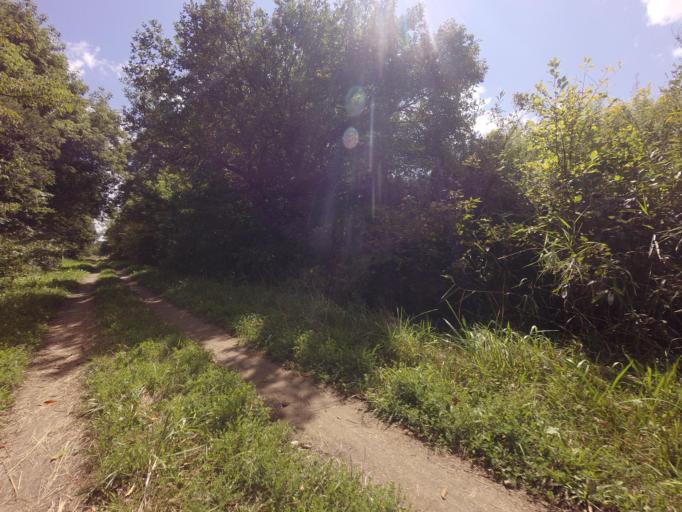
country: CA
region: Ontario
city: Orangeville
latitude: 43.7913
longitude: -80.2642
